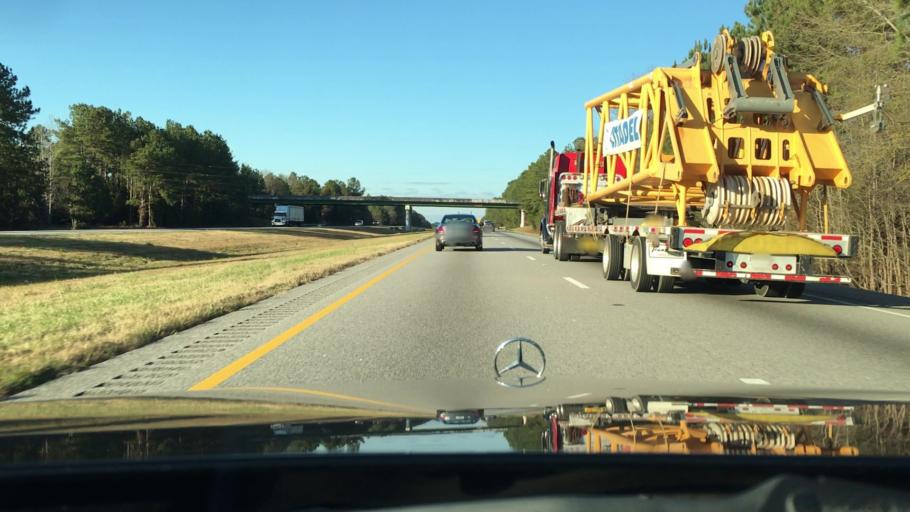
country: US
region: South Carolina
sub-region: Chester County
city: Great Falls
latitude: 34.6770
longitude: -81.0291
